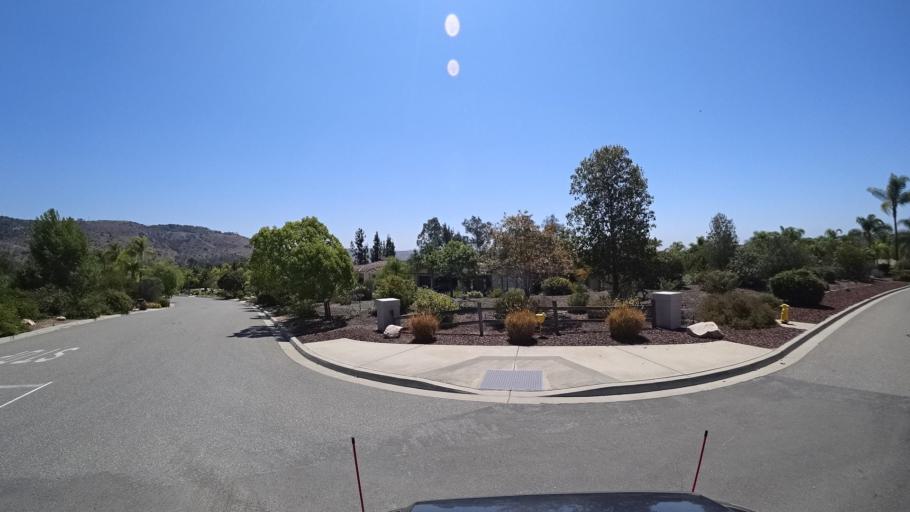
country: US
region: California
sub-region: San Diego County
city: Bonsall
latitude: 33.3261
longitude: -117.1978
